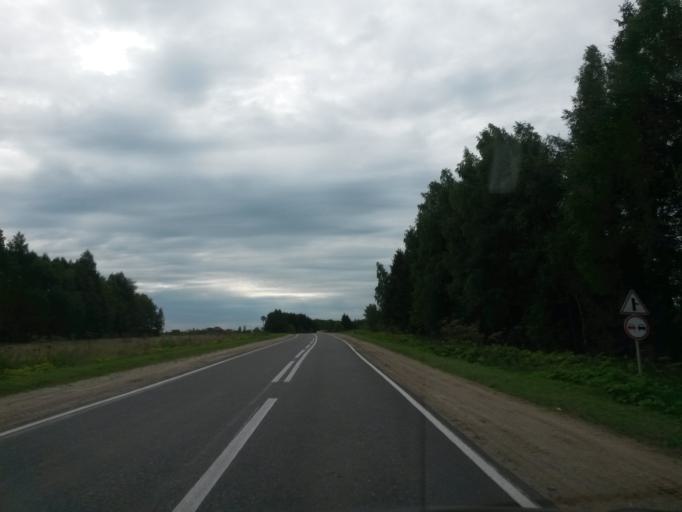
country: RU
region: Jaroslavl
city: Gavrilov-Yam
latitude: 57.3621
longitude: 39.7494
